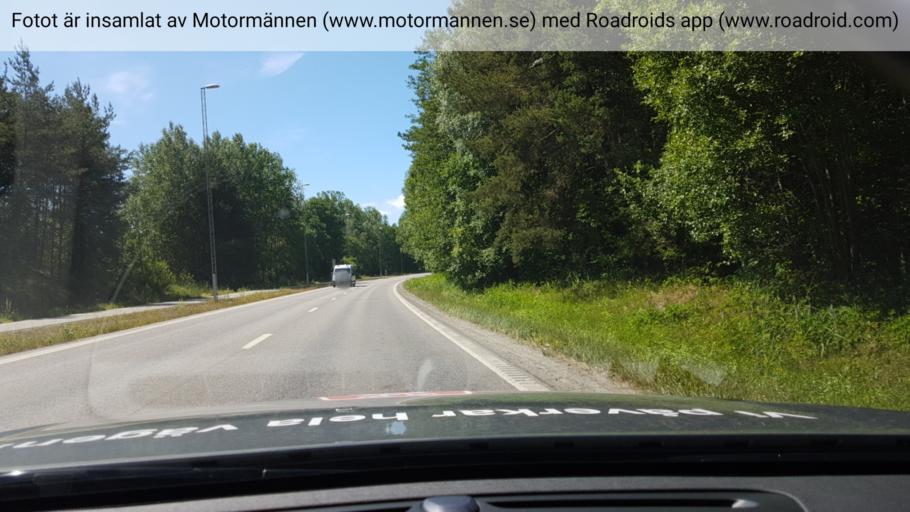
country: SE
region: Stockholm
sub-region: Haninge Kommun
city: Haninge
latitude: 59.1962
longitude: 18.1851
